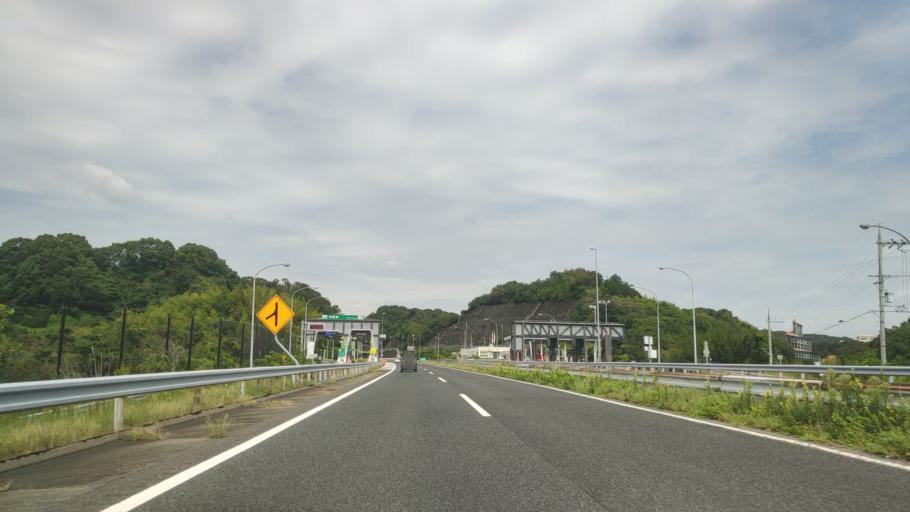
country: JP
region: Wakayama
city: Kainan
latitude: 34.1568
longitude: 135.2318
